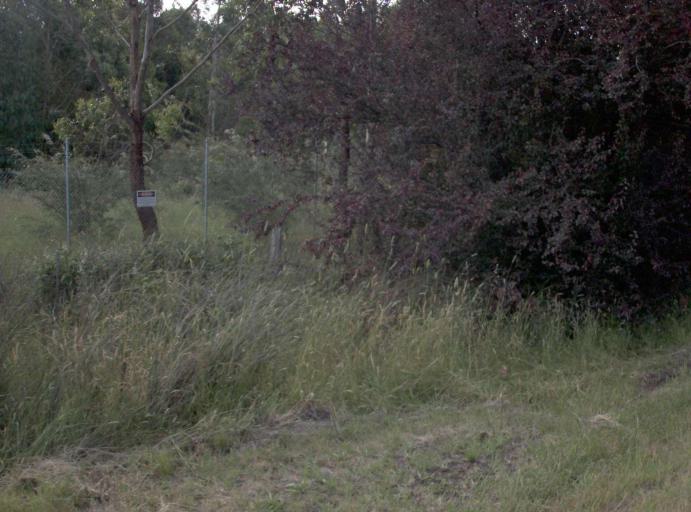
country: AU
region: Victoria
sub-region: Latrobe
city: Morwell
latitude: -38.1991
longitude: 146.4021
